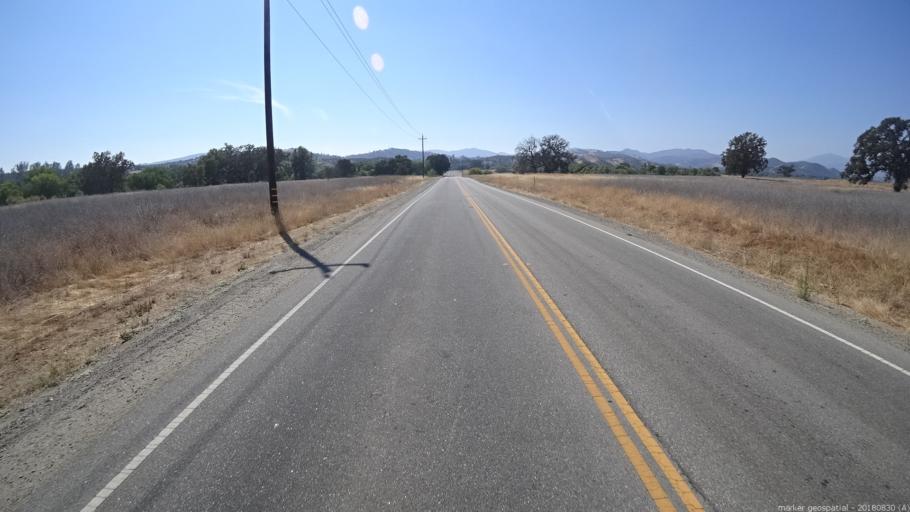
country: US
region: California
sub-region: Monterey County
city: King City
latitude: 35.9855
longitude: -121.2290
